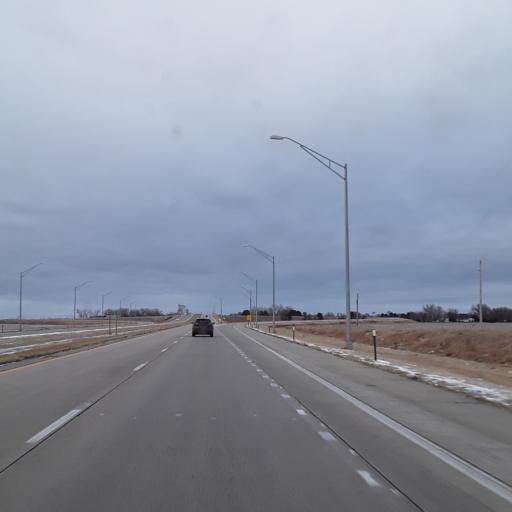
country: US
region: Nebraska
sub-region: Fillmore County
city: Geneva
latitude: 40.6270
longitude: -97.5956
